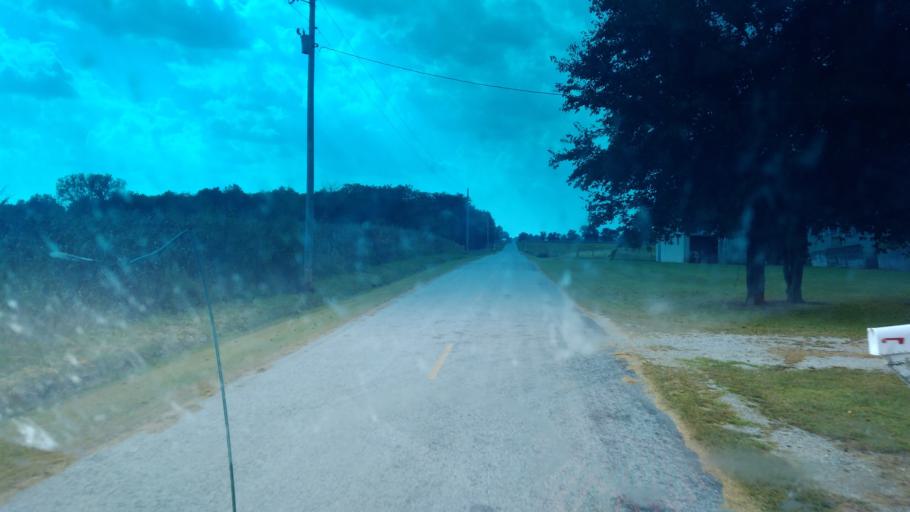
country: US
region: Ohio
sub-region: Hardin County
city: Kenton
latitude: 40.7176
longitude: -83.5964
